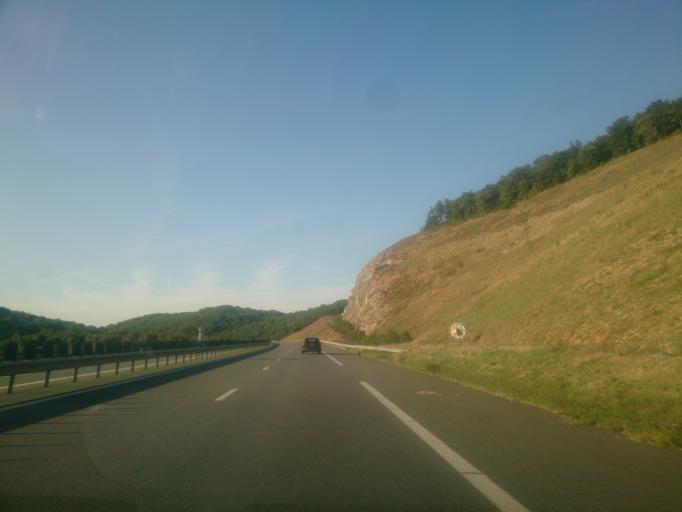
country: FR
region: Midi-Pyrenees
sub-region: Departement du Lot
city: Souillac
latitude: 44.8313
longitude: 1.4959
